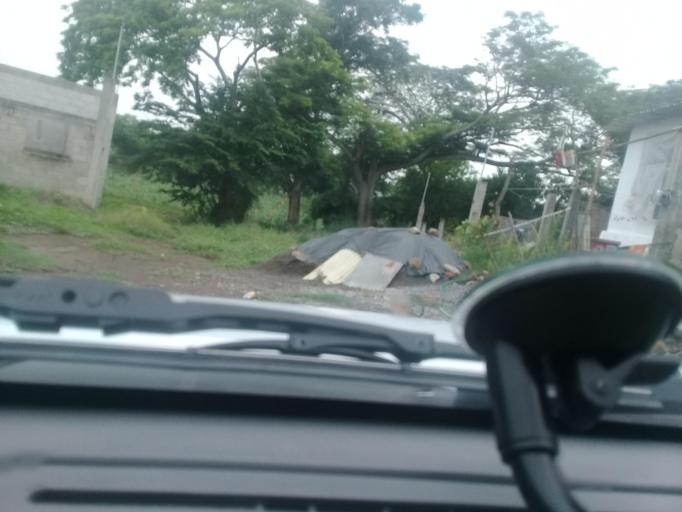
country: MX
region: Veracruz
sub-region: Puente Nacional
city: Cabezas
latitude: 19.3751
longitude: -96.3855
